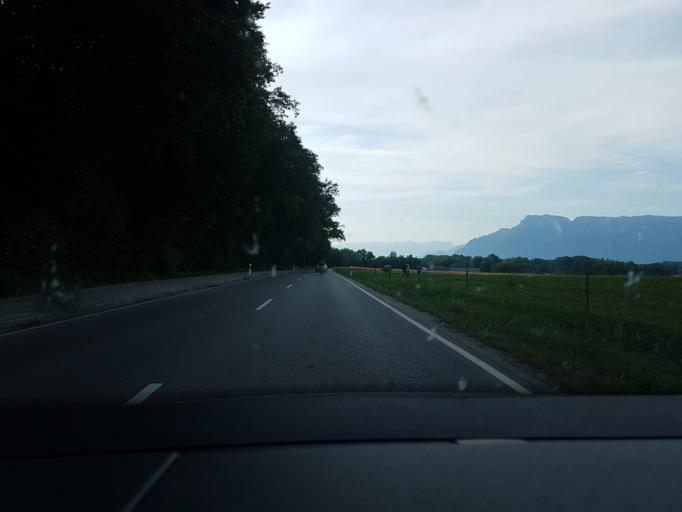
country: DE
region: Bavaria
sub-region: Upper Bavaria
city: Ainring
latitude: 47.8520
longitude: 12.9400
